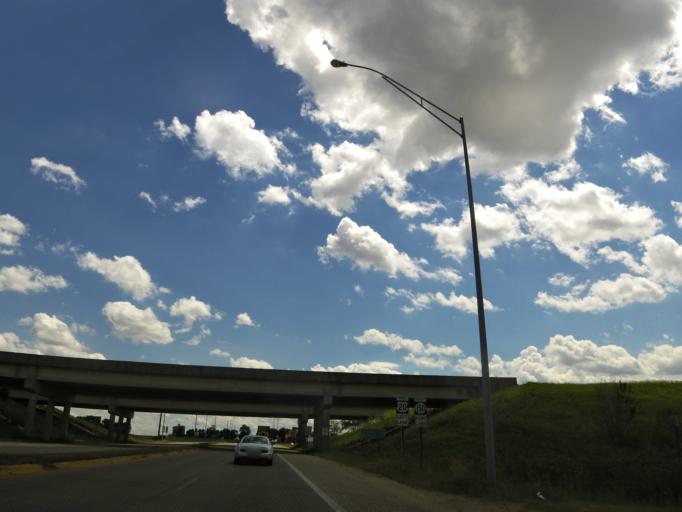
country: US
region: Iowa
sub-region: Buchanan County
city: Independence
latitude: 42.4494
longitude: -91.8903
